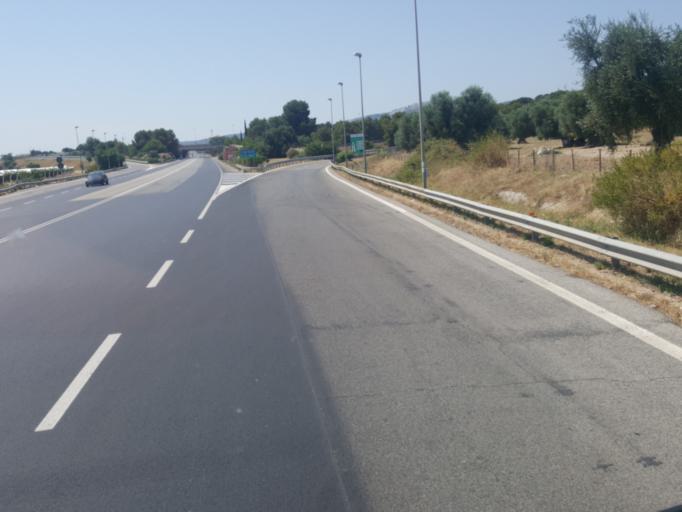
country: IT
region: Apulia
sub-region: Provincia di Taranto
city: Massafra
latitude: 40.5953
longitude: 17.0880
